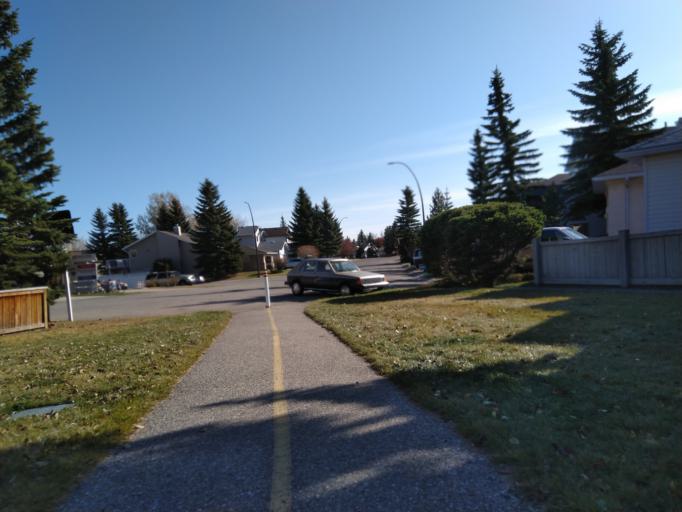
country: CA
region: Alberta
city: Calgary
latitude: 51.1421
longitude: -114.1181
